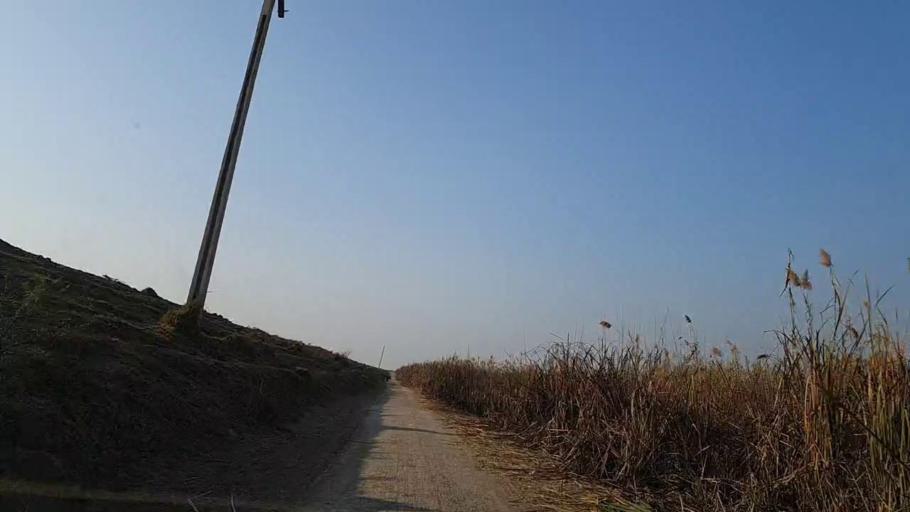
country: PK
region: Sindh
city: Sakrand
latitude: 26.0965
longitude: 68.3708
